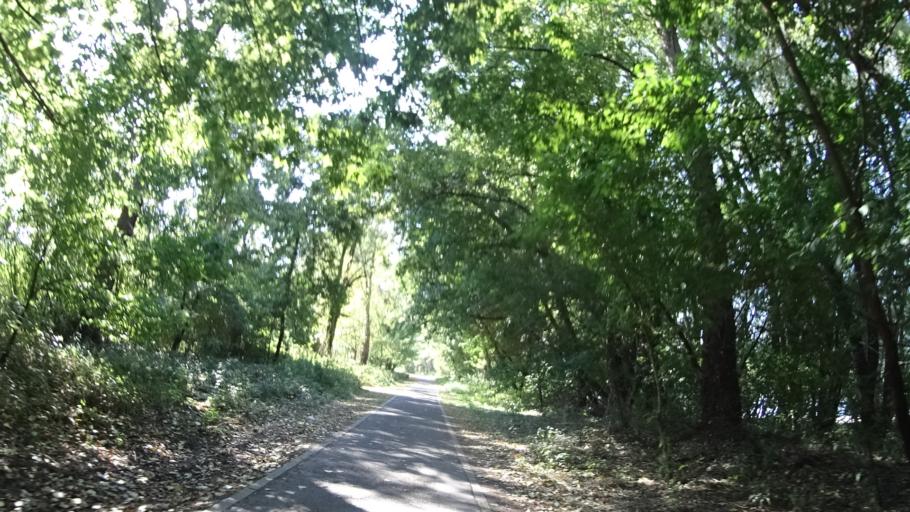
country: HU
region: Komarom-Esztergom
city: Esztergom
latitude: 47.8156
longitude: 18.7915
